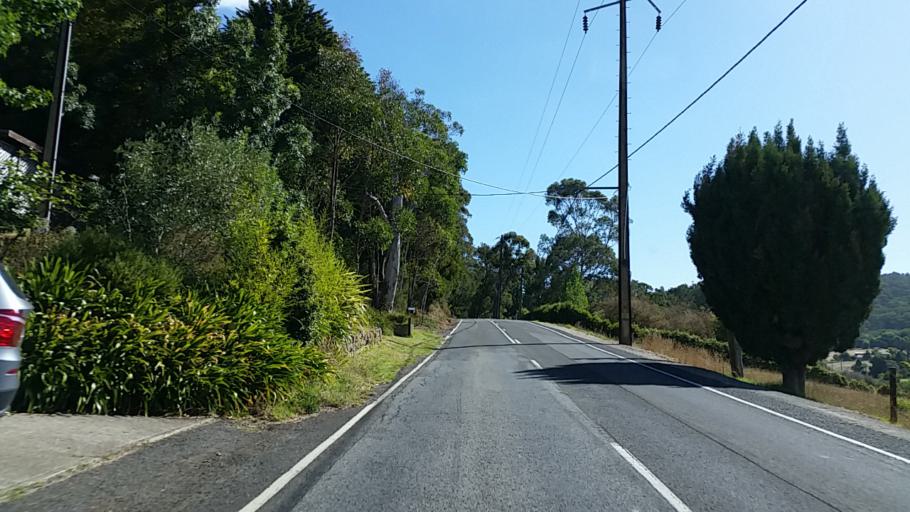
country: AU
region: South Australia
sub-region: Adelaide Hills
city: Bridgewater
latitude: -34.9805
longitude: 138.7283
